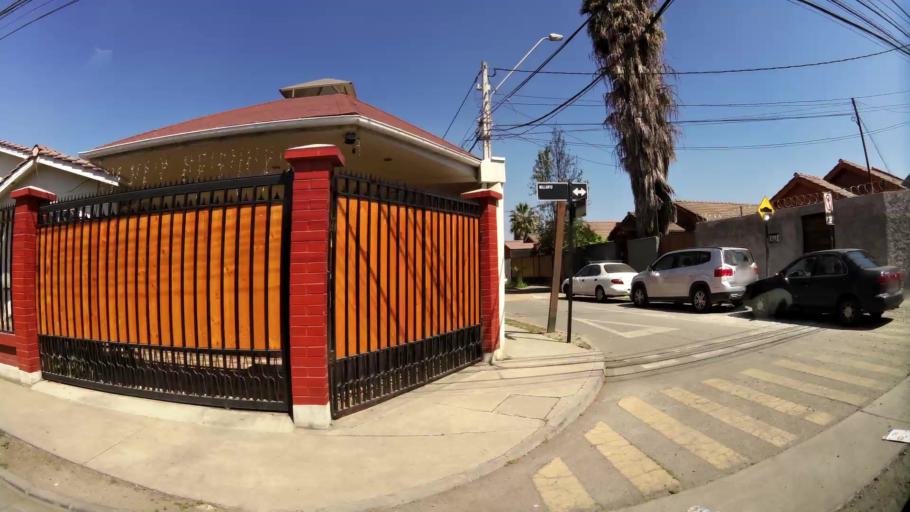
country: CL
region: Santiago Metropolitan
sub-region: Provincia de Santiago
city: Lo Prado
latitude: -33.3522
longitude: -70.7263
